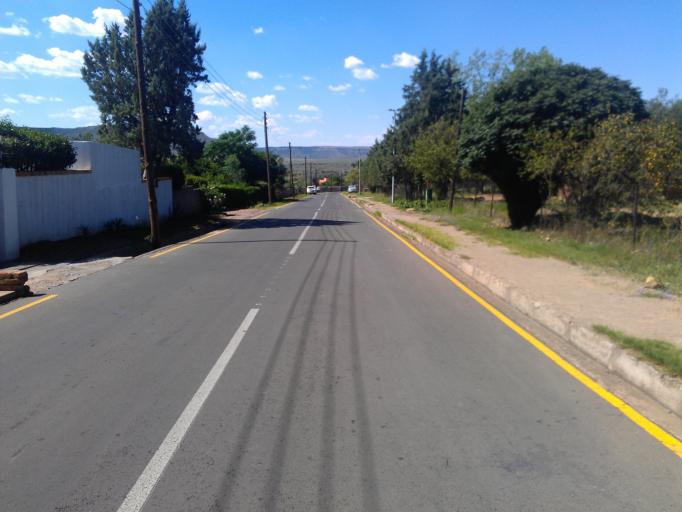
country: LS
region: Maseru
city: Maseru
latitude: -29.3038
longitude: 27.4685
